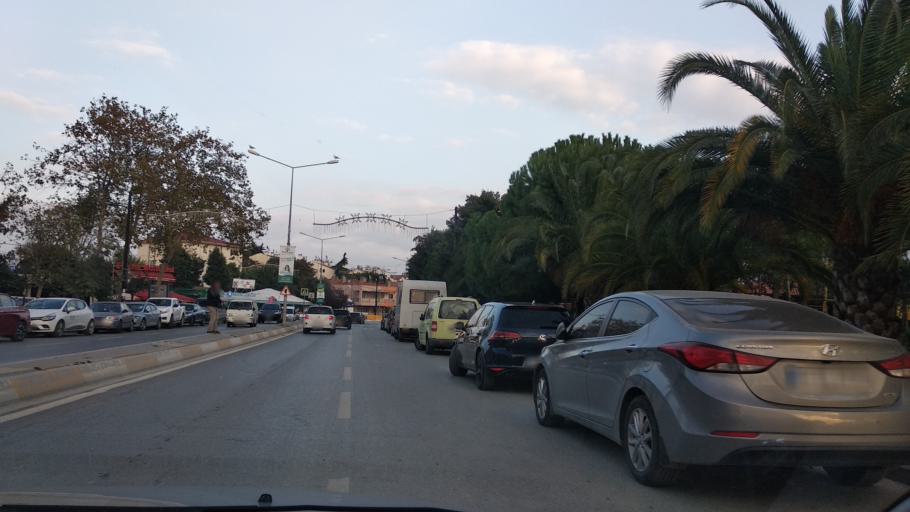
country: TR
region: Istanbul
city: Icmeler
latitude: 40.8149
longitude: 29.3051
